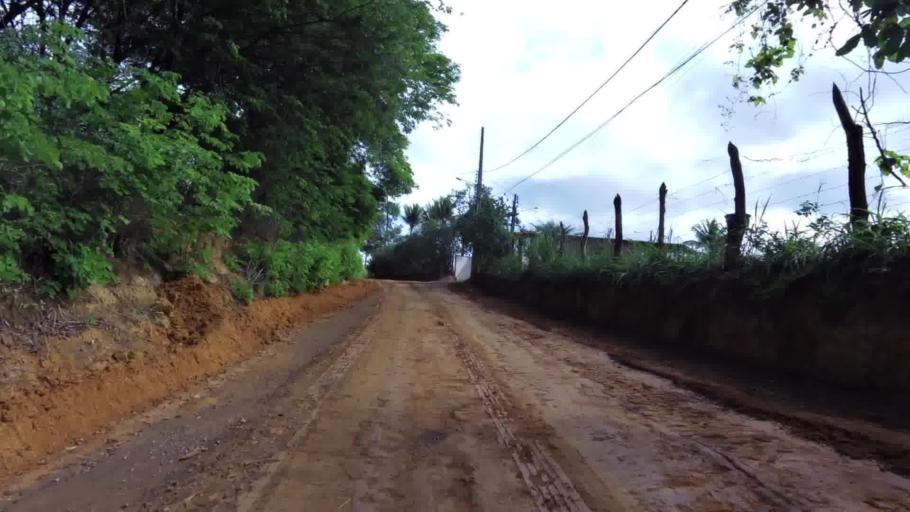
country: BR
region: Espirito Santo
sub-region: Piuma
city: Piuma
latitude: -20.8103
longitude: -40.6653
